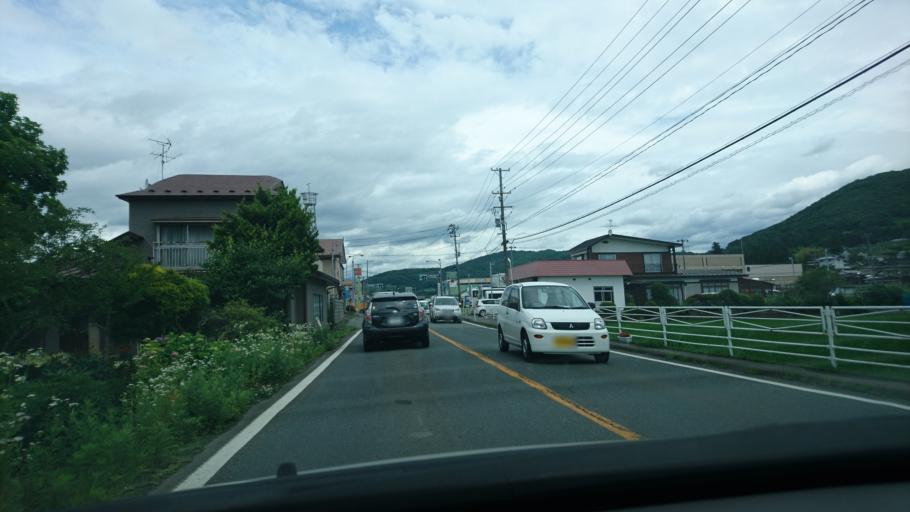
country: JP
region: Iwate
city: Morioka-shi
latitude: 39.6421
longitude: 141.1854
